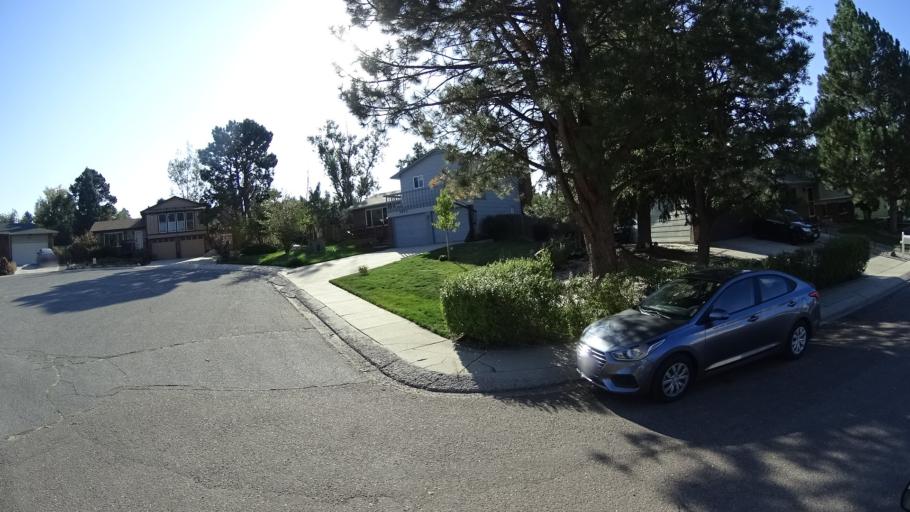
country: US
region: Colorado
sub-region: El Paso County
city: Cimarron Hills
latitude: 38.8895
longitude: -104.7341
